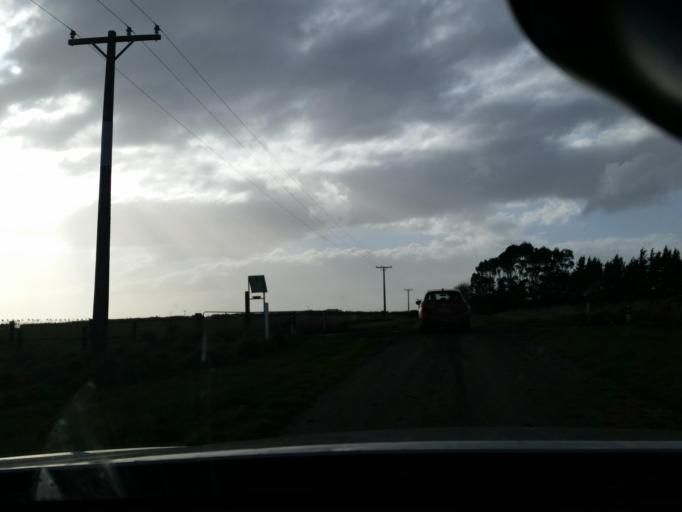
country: NZ
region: Southland
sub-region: Southland District
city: Winton
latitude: -46.2429
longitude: 168.3222
